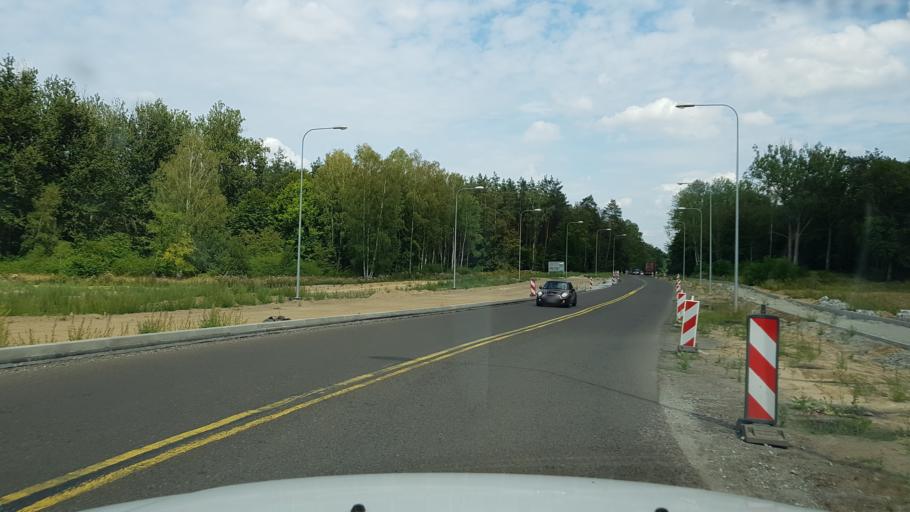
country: PL
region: West Pomeranian Voivodeship
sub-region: Powiat walecki
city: Walcz
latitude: 53.2862
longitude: 16.5086
